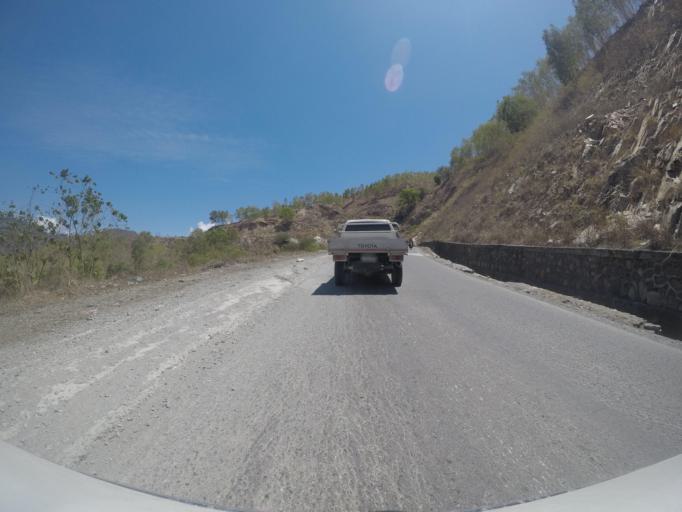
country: TL
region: Dili
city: Dili
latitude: -8.5600
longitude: 125.6405
